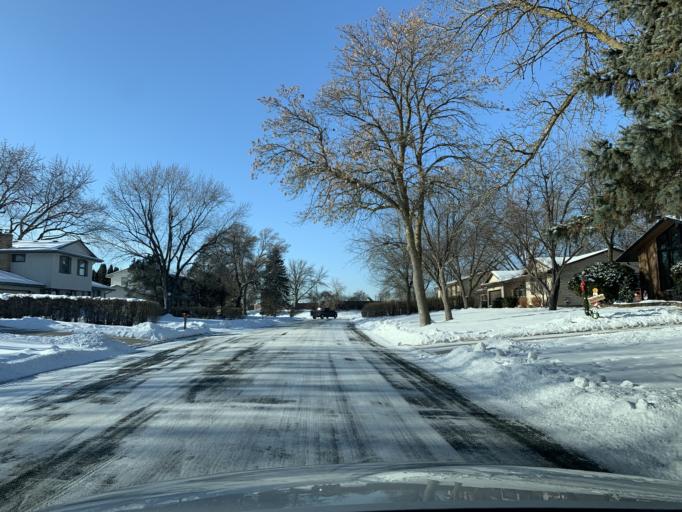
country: US
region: Minnesota
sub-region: Scott County
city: Savage
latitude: 44.8235
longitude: -93.3449
